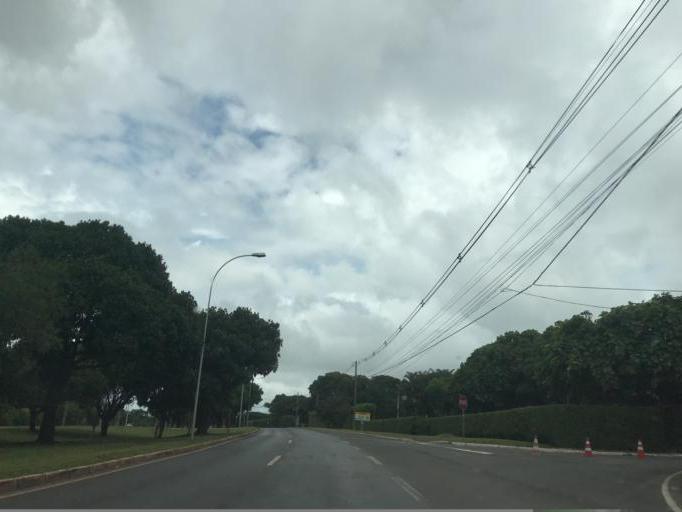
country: BR
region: Federal District
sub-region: Brasilia
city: Brasilia
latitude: -15.8436
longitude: -47.8521
